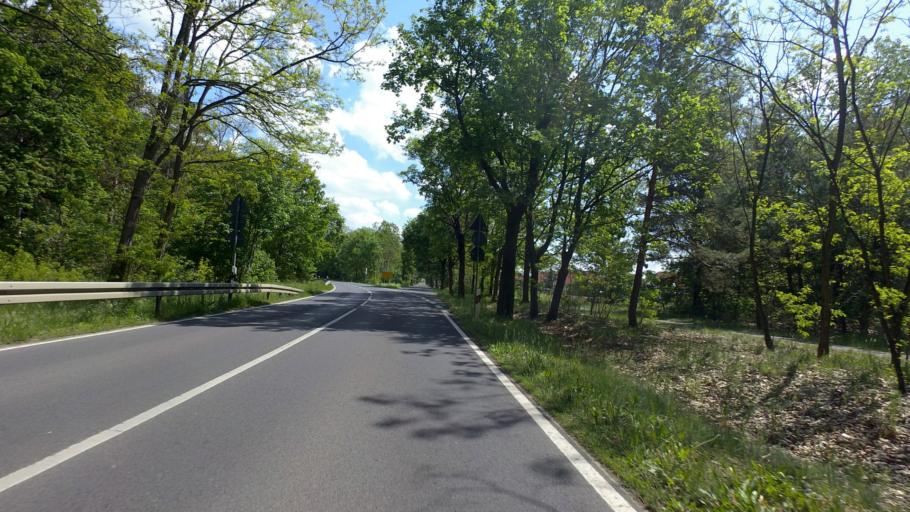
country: DE
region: Brandenburg
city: Luebben
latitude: 51.9440
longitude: 13.9707
